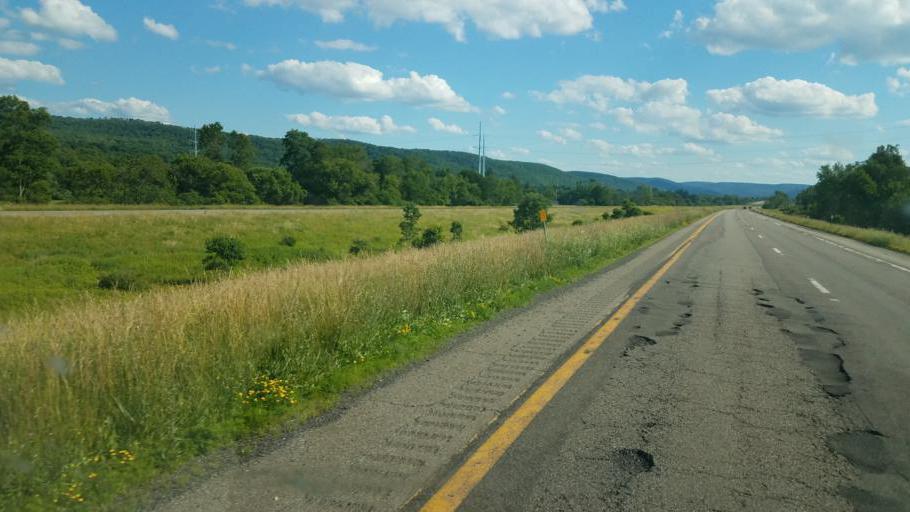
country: US
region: New York
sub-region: Cattaraugus County
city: Olean
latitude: 42.1475
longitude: -78.4077
